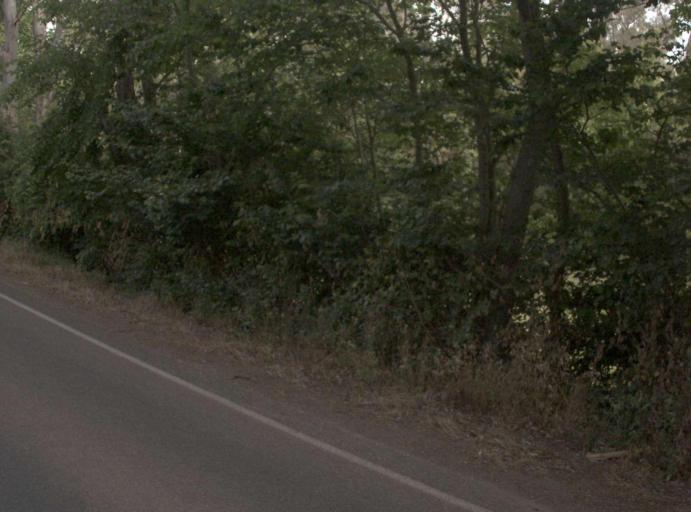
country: AU
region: Victoria
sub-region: Wellington
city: Sale
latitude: -37.9652
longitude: 146.9682
